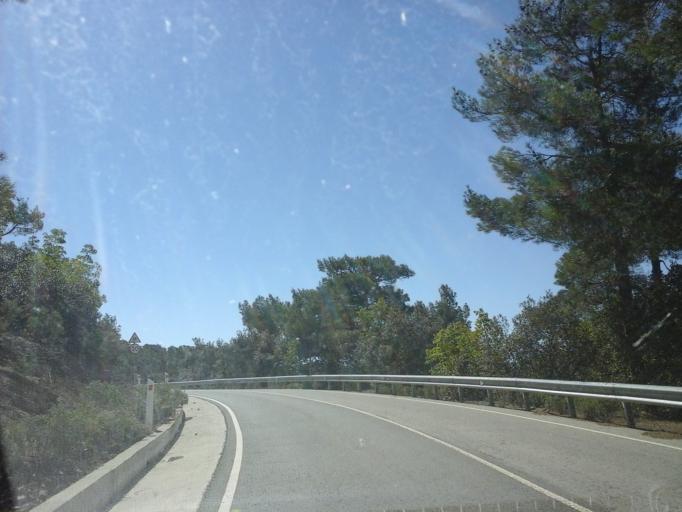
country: CY
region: Lefkosia
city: Kakopetria
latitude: 34.9150
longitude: 32.8302
